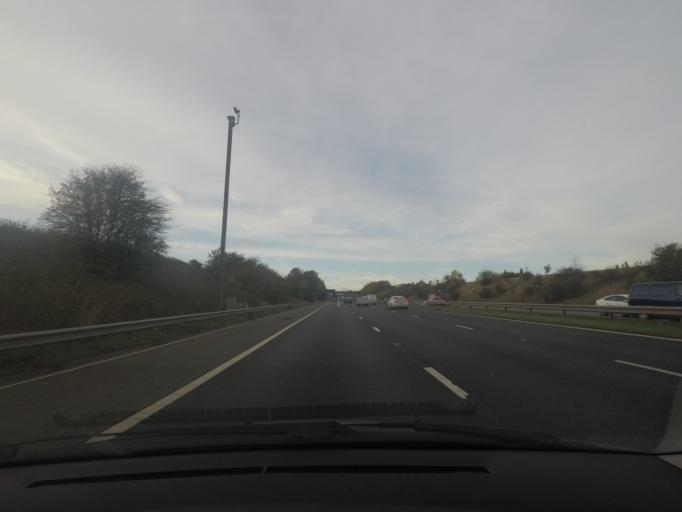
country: GB
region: England
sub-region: Barnsley
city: Dodworth
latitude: 53.5448
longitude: -1.5127
